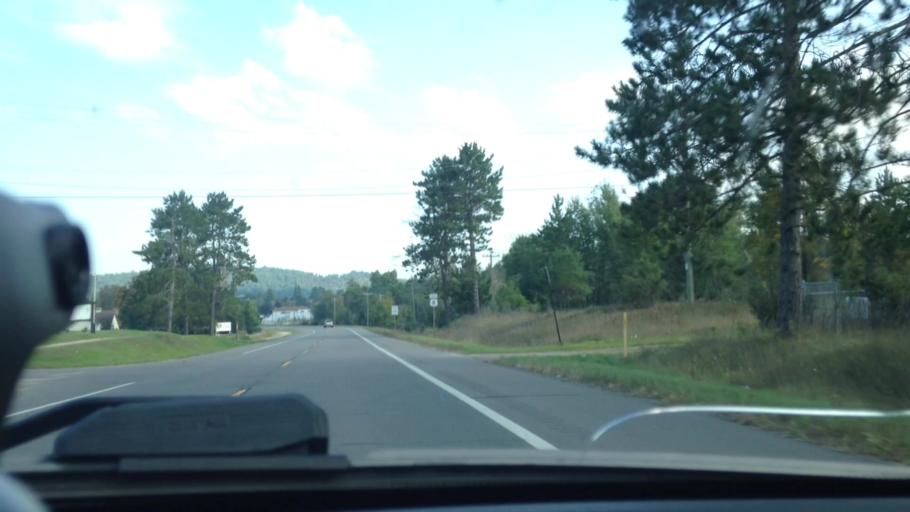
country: US
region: Michigan
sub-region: Dickinson County
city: Norway
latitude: 45.7761
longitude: -87.9090
